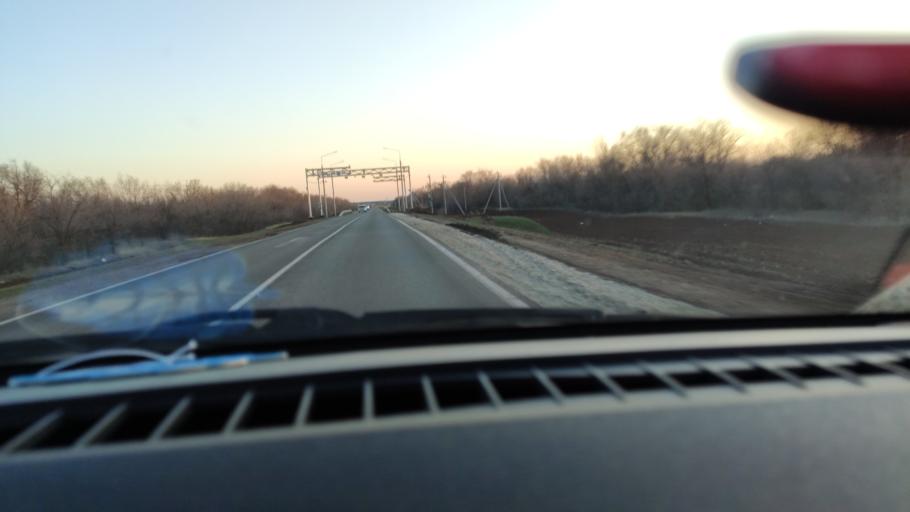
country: RU
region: Saratov
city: Privolzhskiy
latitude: 51.3193
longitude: 46.0233
